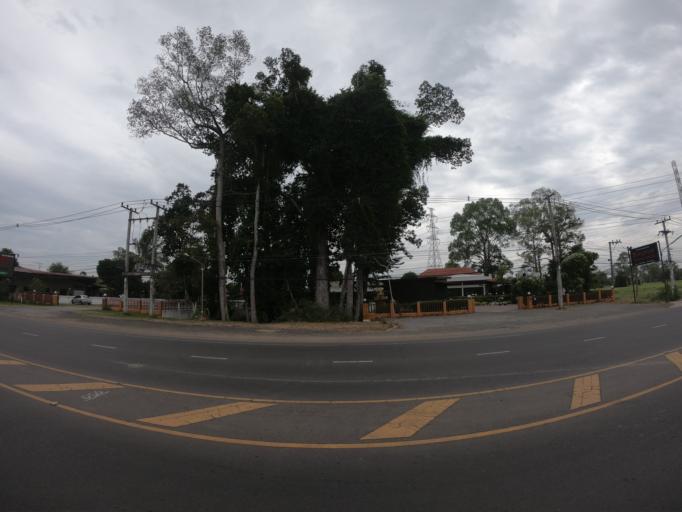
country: TH
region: Roi Et
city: Roi Et
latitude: 16.0738
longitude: 103.6841
